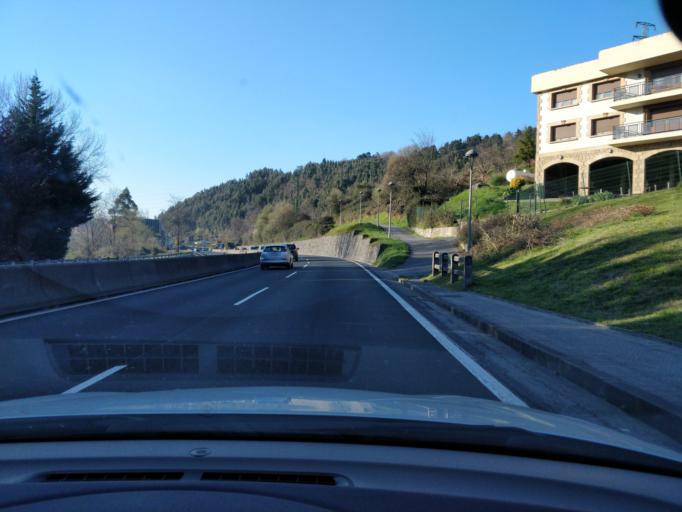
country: ES
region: Basque Country
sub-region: Bizkaia
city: Basauri
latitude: 43.2423
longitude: -2.8757
